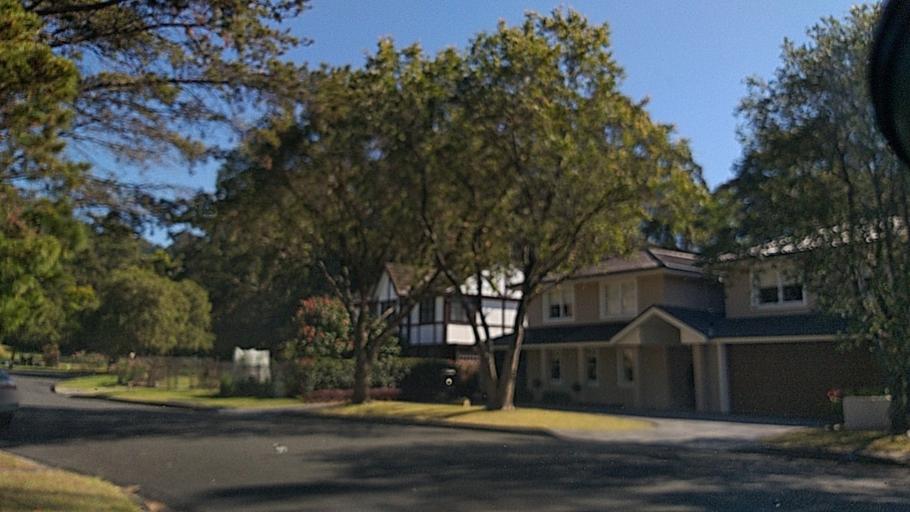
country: AU
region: New South Wales
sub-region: Wollongong
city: Mount Ousley
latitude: -34.3950
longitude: 150.8770
